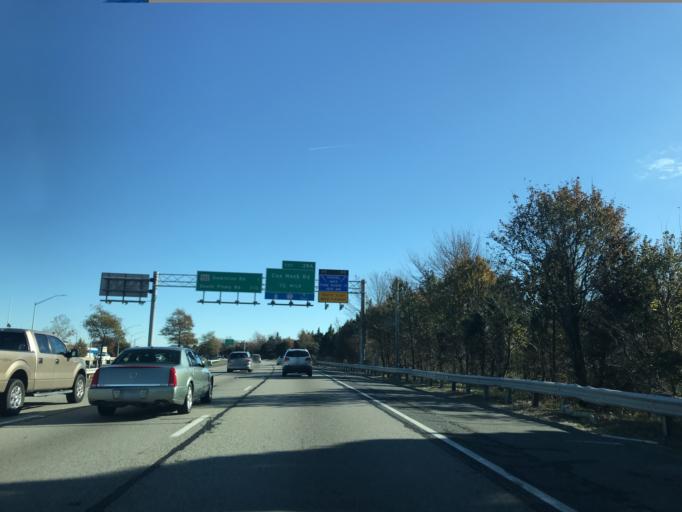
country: US
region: Maryland
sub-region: Queen Anne's County
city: Chester
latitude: 38.9745
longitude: -76.3003
